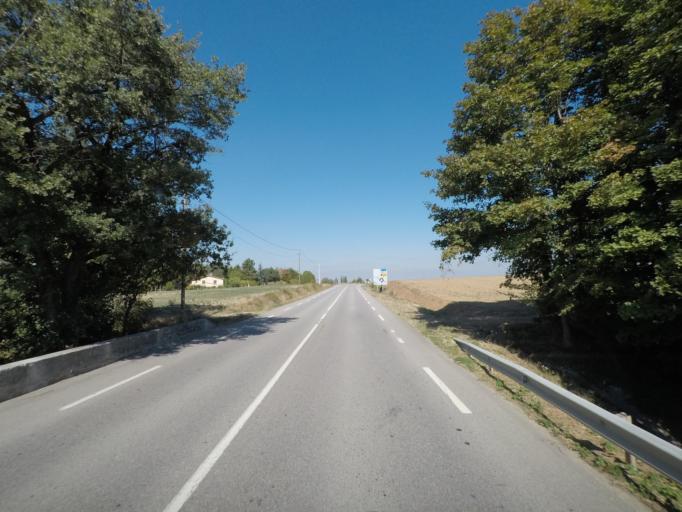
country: FR
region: Rhone-Alpes
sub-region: Departement de la Drome
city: Montmeyran
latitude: 44.8397
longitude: 5.0096
